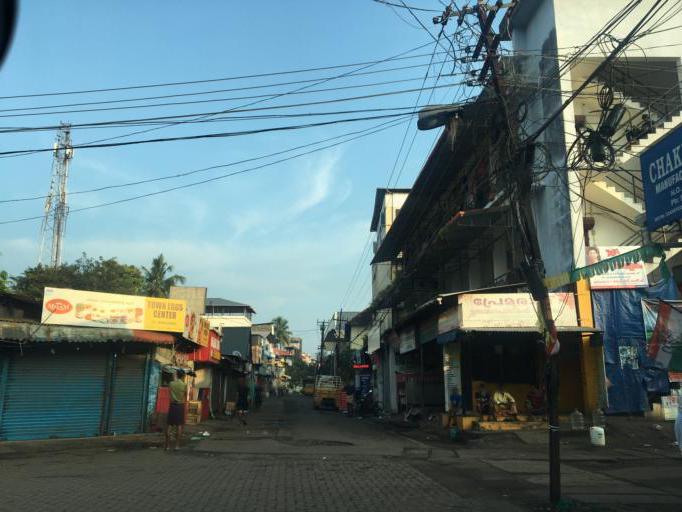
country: IN
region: Kerala
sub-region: Ernakulam
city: Cochin
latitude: 9.9817
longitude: 76.2780
